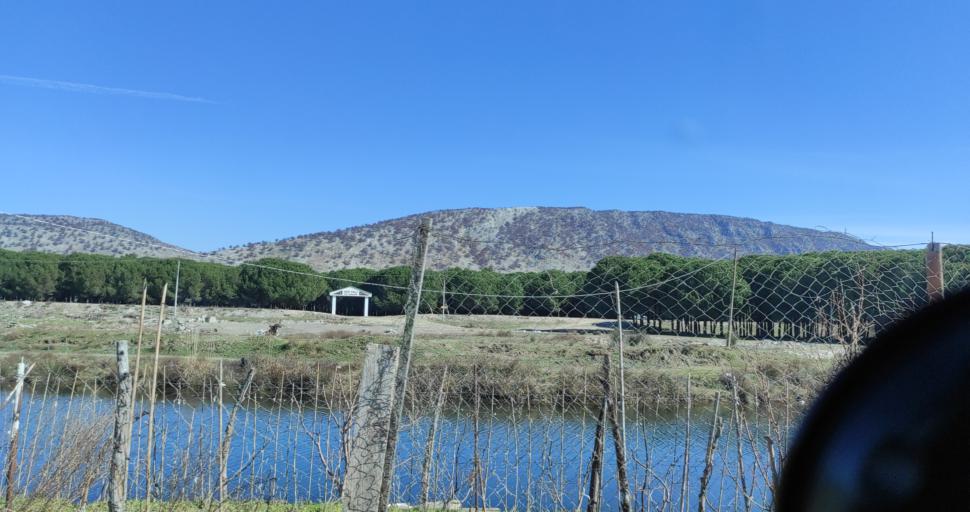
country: AL
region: Shkoder
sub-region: Rrethi i Shkodres
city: Velipoje
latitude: 41.8644
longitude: 19.4412
